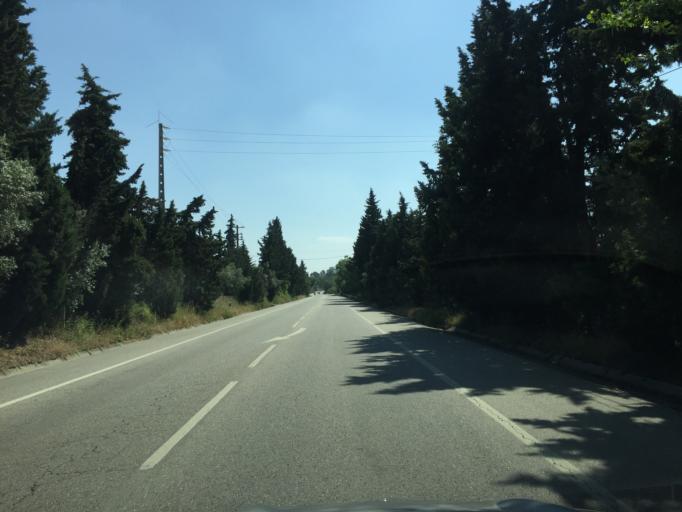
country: PT
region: Santarem
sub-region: Golega
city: Golega
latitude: 39.3841
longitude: -8.4509
